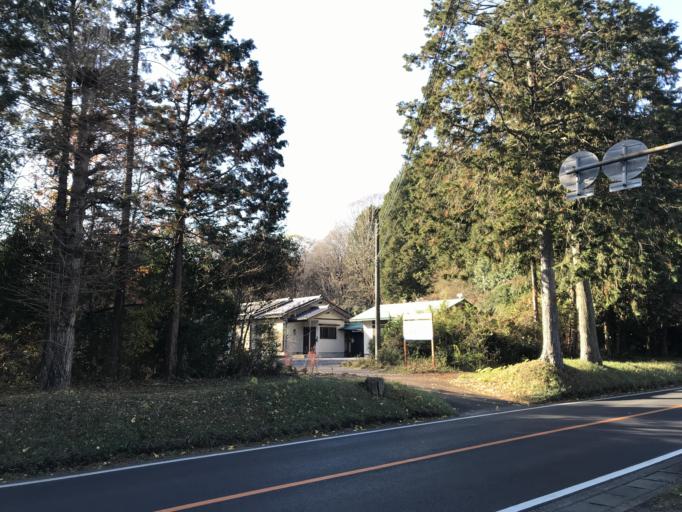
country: JP
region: Tochigi
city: Kanuma
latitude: 36.6138
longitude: 139.7384
